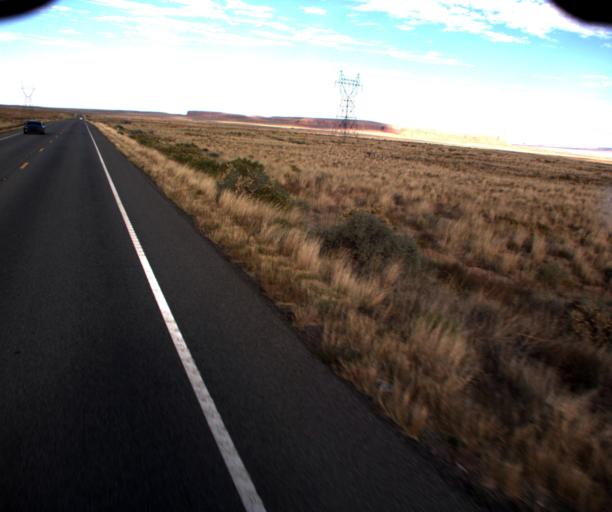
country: US
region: Arizona
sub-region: Apache County
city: Lukachukai
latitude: 36.9351
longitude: -109.2337
